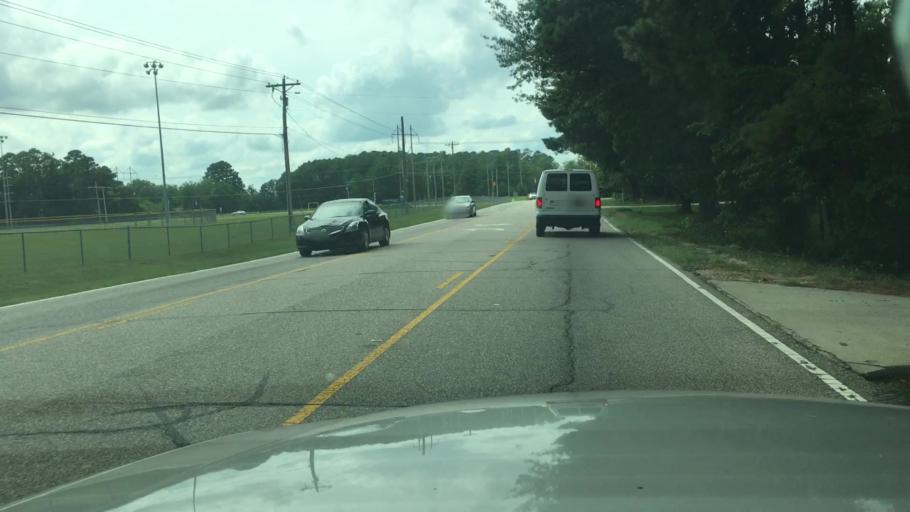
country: US
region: North Carolina
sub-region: Cumberland County
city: Hope Mills
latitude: 35.0025
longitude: -78.9912
